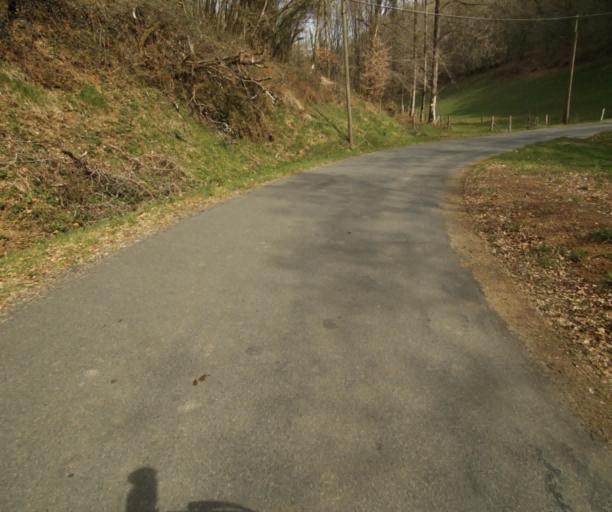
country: FR
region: Limousin
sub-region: Departement de la Correze
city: Naves
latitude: 45.3506
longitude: 1.8121
